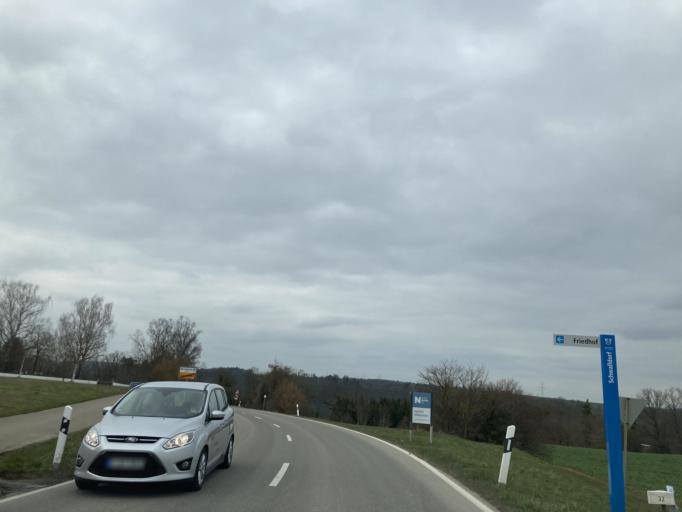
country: DE
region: Baden-Wuerttemberg
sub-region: Tuebingen Region
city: Hirrlingen
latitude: 48.4524
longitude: 8.8803
